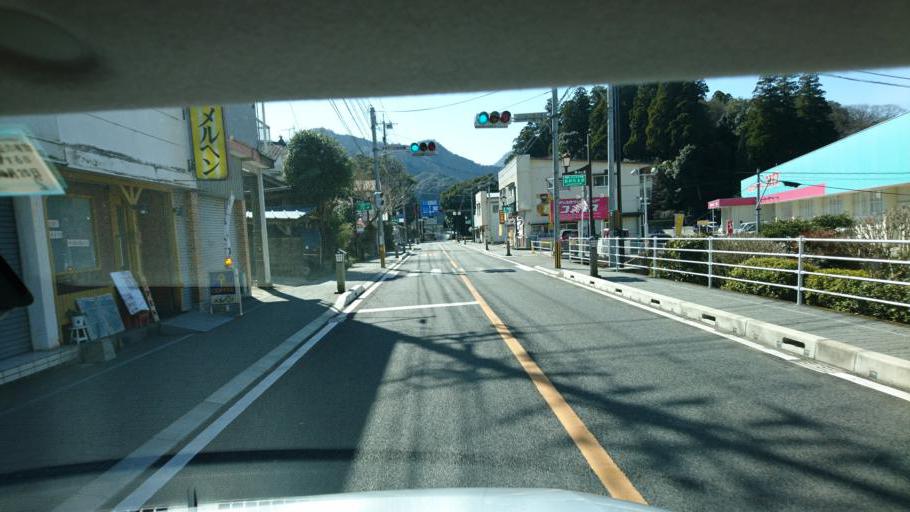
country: JP
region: Oita
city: Takedamachi
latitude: 32.7073
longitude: 131.3044
